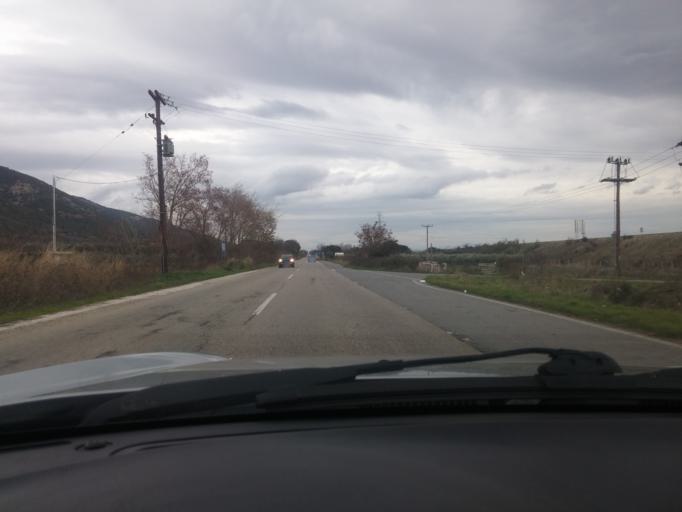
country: GR
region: East Macedonia and Thrace
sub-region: Nomos Rodopis
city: Iasmos
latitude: 41.1203
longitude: 25.0898
